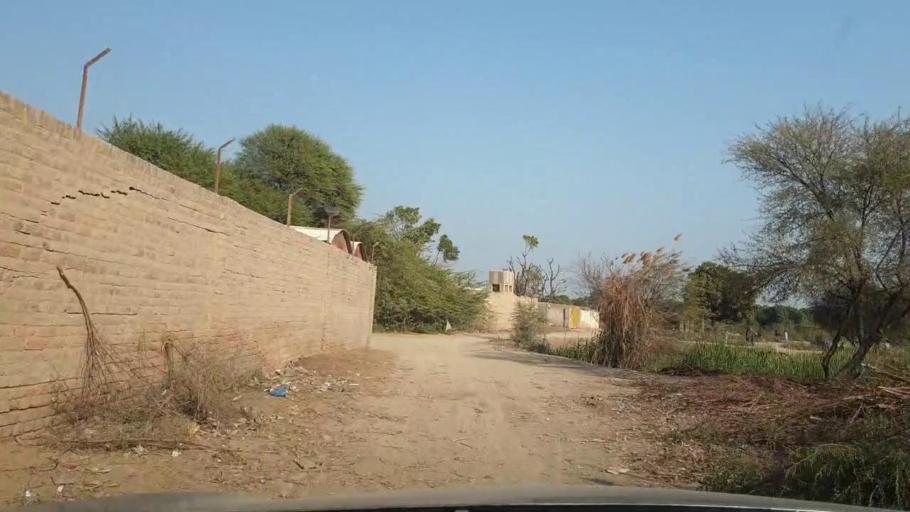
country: PK
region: Sindh
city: Tando Allahyar
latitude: 25.5816
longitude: 68.7641
